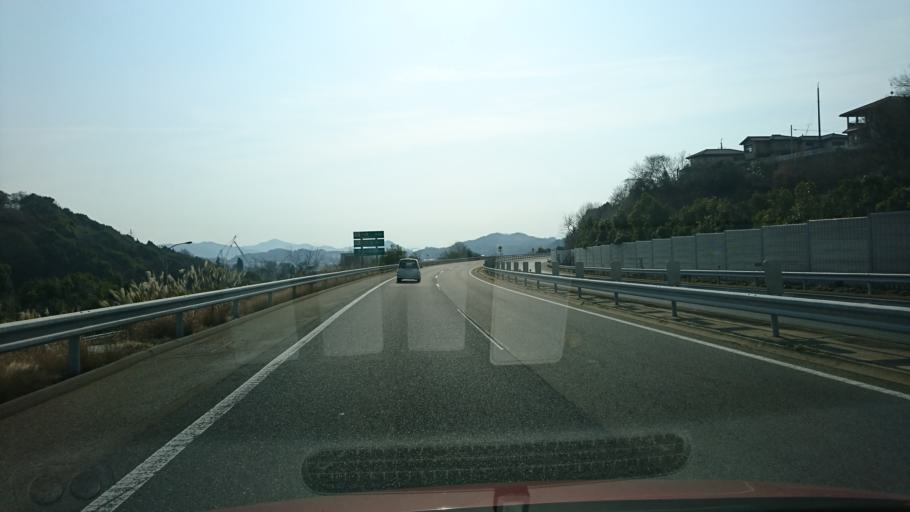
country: JP
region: Hiroshima
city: Onomichi
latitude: 34.4170
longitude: 133.2200
